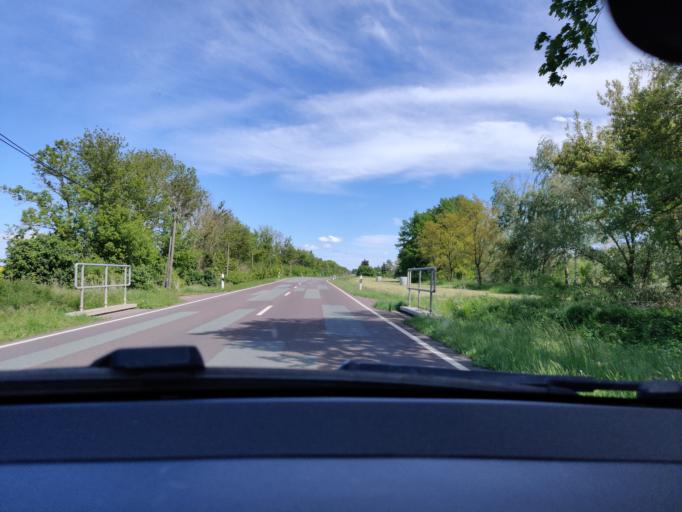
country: DE
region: Saxony-Anhalt
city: Mockern
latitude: 52.1195
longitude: 11.9218
